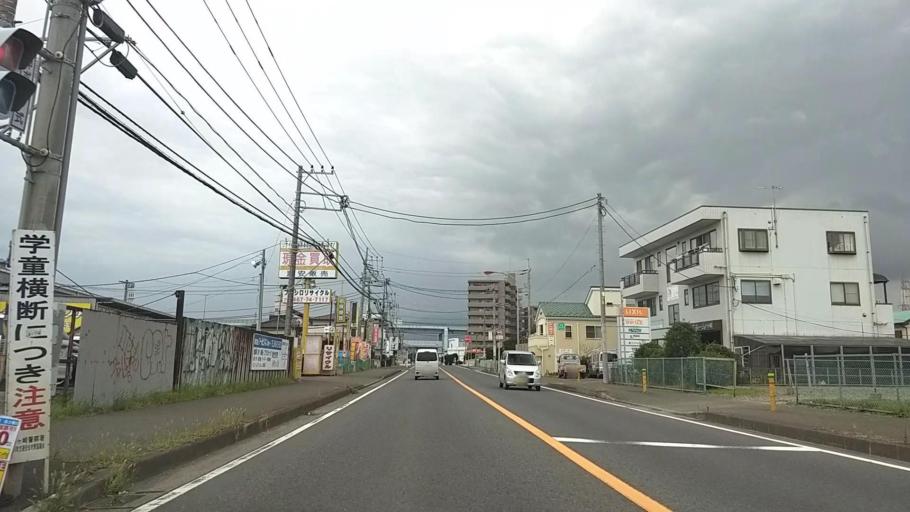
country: JP
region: Kanagawa
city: Chigasaki
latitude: 35.3713
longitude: 139.3783
